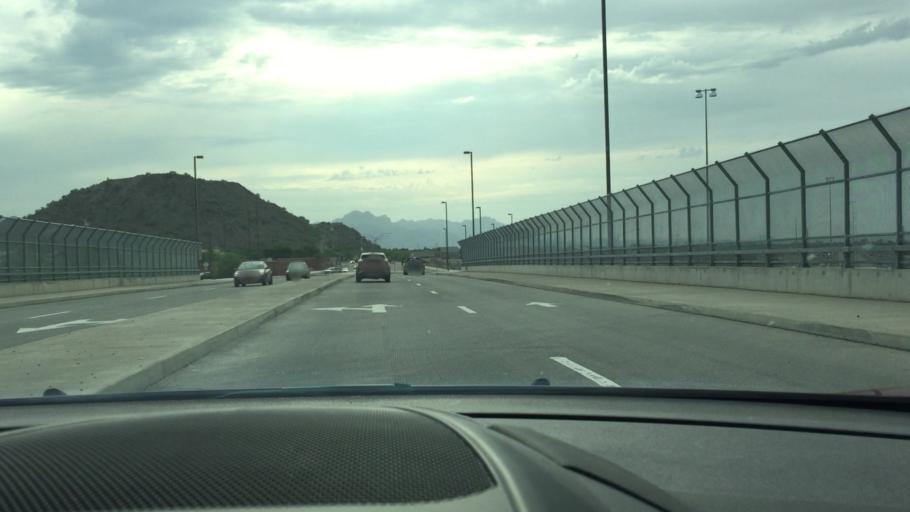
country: US
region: Arizona
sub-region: Pinal County
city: Apache Junction
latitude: 33.4399
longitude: -111.6513
